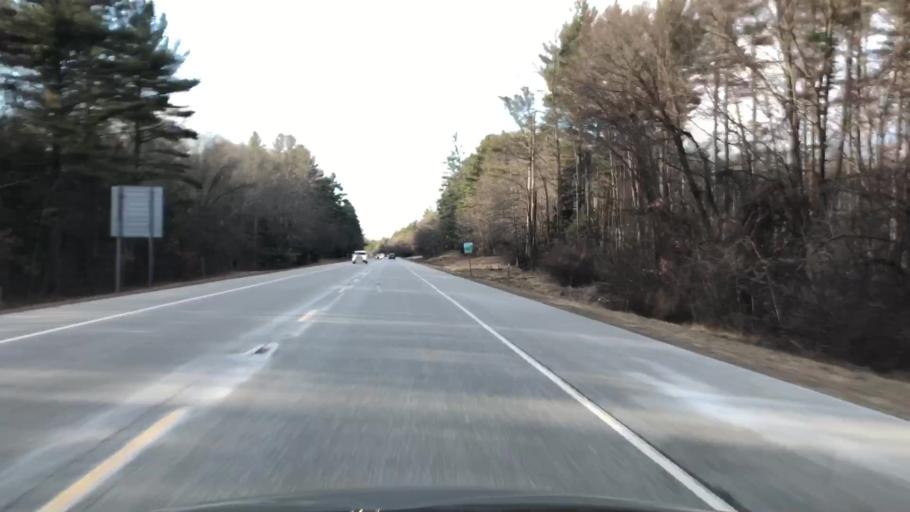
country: US
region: New Hampshire
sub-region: Hillsborough County
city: Milford
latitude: 42.8273
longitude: -71.6685
